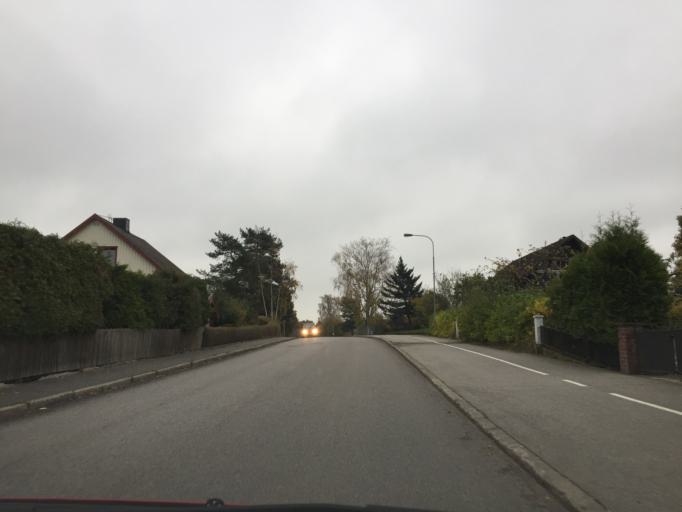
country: SE
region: Vaestra Goetaland
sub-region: Trollhattan
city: Trollhattan
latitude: 58.2665
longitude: 12.2835
